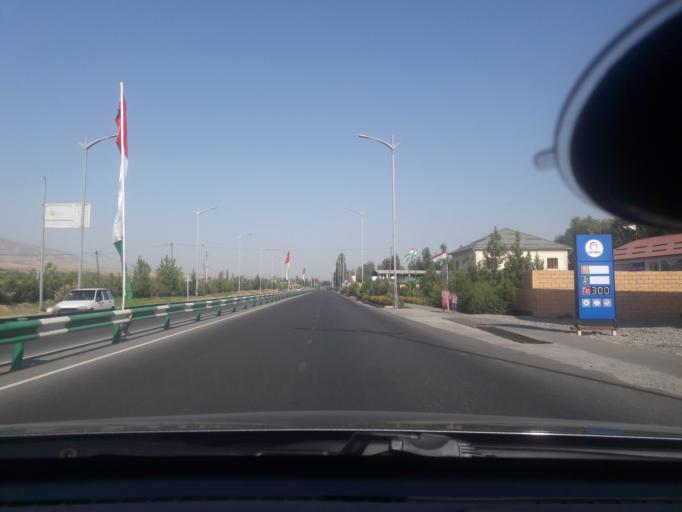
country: TJ
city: Shahrinav
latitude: 38.5765
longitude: 68.3358
